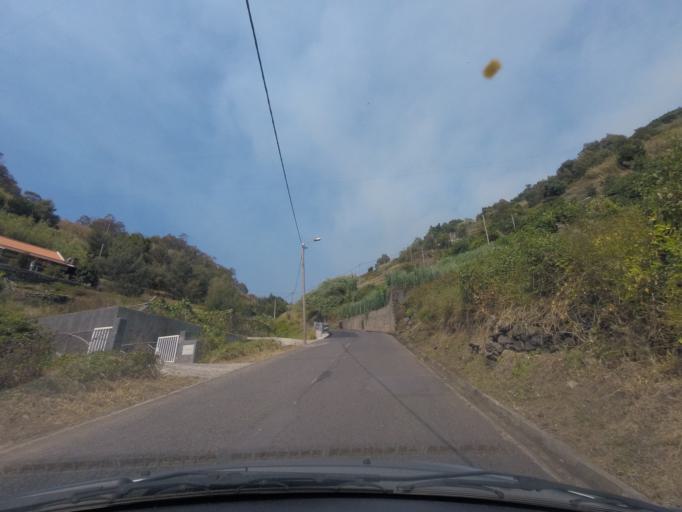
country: PT
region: Madeira
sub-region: Ribeira Brava
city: Campanario
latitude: 32.6907
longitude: -17.0669
